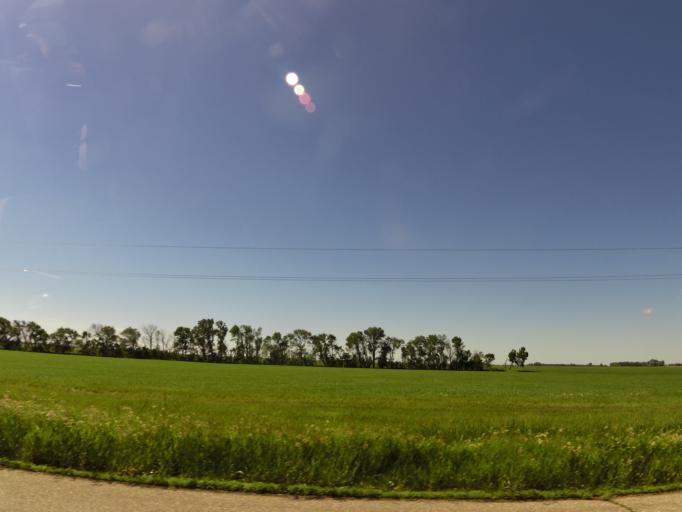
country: US
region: Minnesota
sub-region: Polk County
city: Crookston
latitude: 47.7604
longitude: -96.4695
